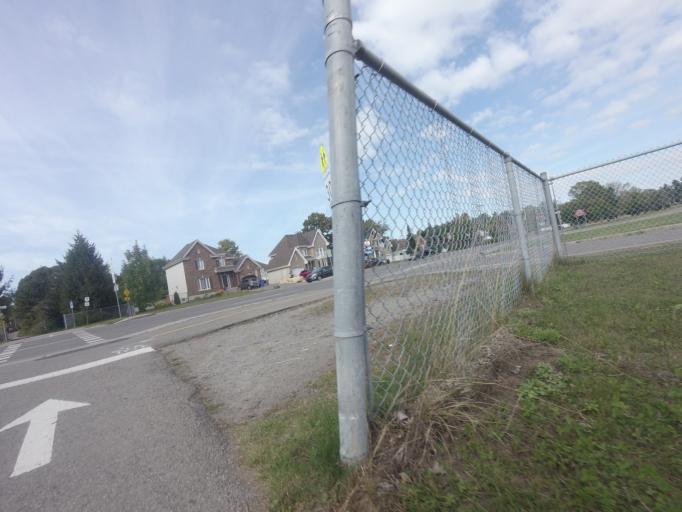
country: CA
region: Quebec
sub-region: Laurentides
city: Blainville
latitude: 45.6983
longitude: -73.9004
